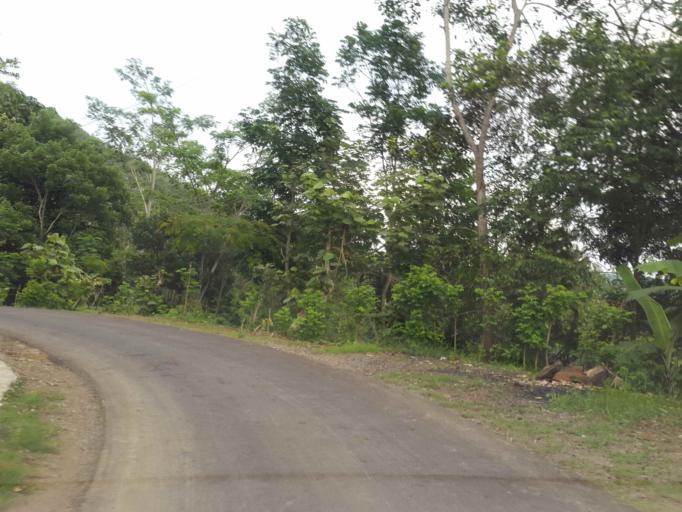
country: ID
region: Central Java
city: Jambuluwuk
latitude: -7.3337
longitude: 108.9218
